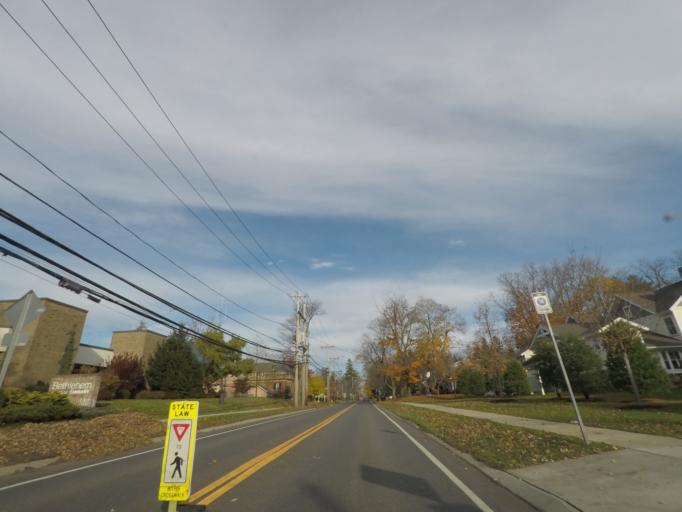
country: US
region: New York
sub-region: Albany County
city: Delmar
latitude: 42.6191
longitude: -73.8413
